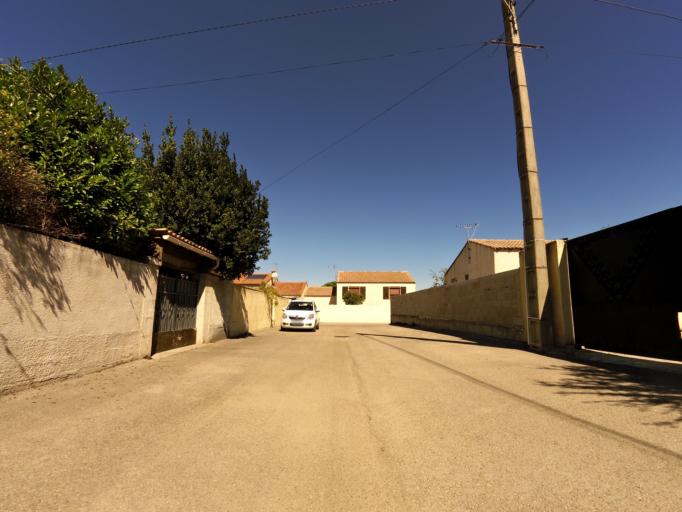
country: FR
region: Languedoc-Roussillon
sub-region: Departement du Gard
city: Codognan
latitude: 43.7275
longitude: 4.2189
